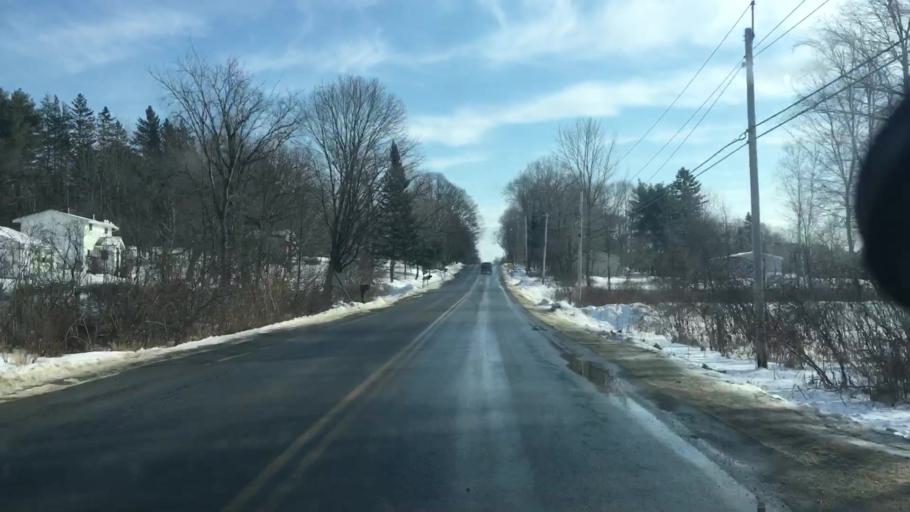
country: US
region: Maine
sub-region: Penobscot County
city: Bangor
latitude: 44.8501
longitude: -68.8418
